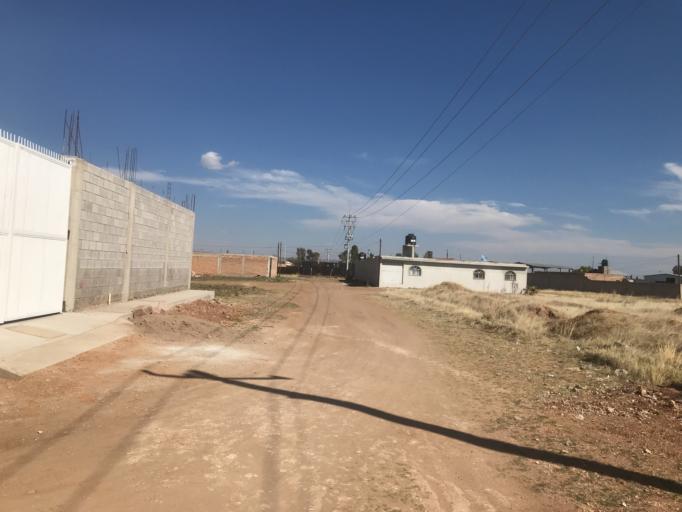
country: MX
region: Durango
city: Victoria de Durango
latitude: 24.0243
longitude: -104.5881
